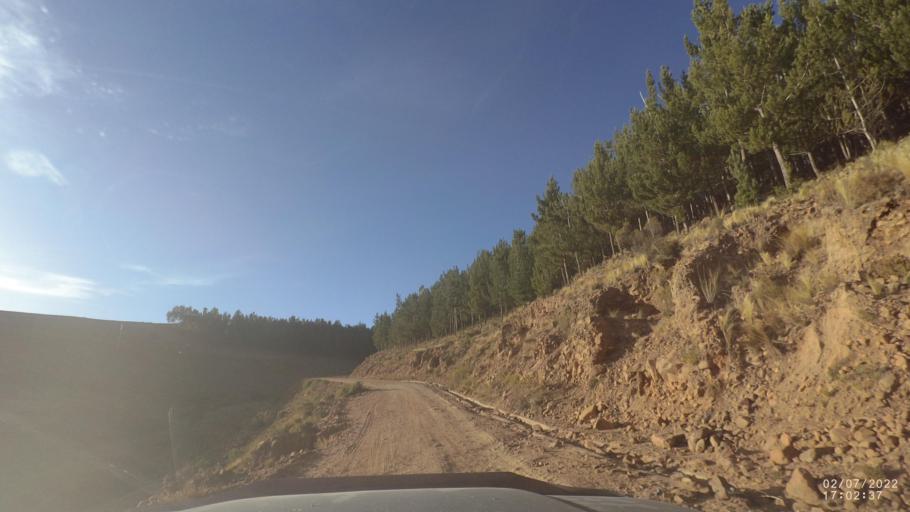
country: BO
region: Cochabamba
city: Irpa Irpa
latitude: -17.9248
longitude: -66.5546
